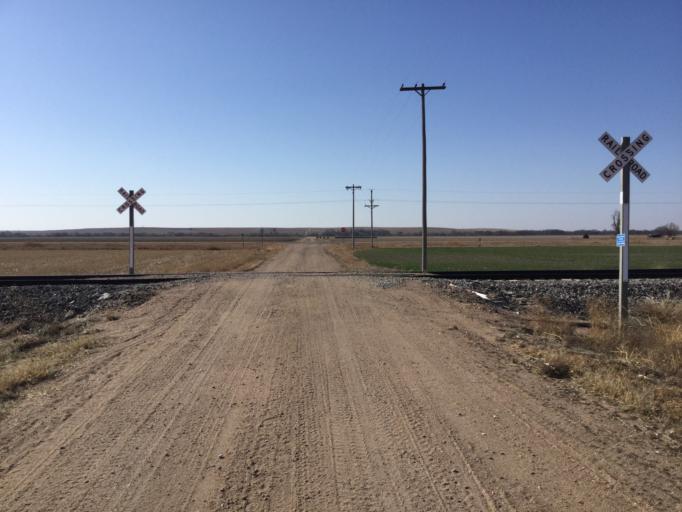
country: US
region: Kansas
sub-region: Rush County
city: La Crosse
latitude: 38.4665
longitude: -99.2720
